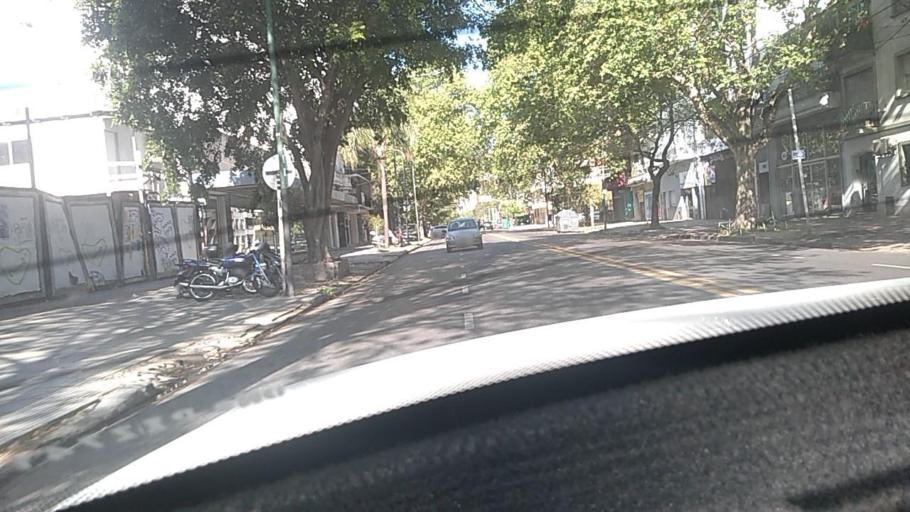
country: AR
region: Buenos Aires F.D.
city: Villa Santa Rita
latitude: -34.6025
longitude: -58.5067
